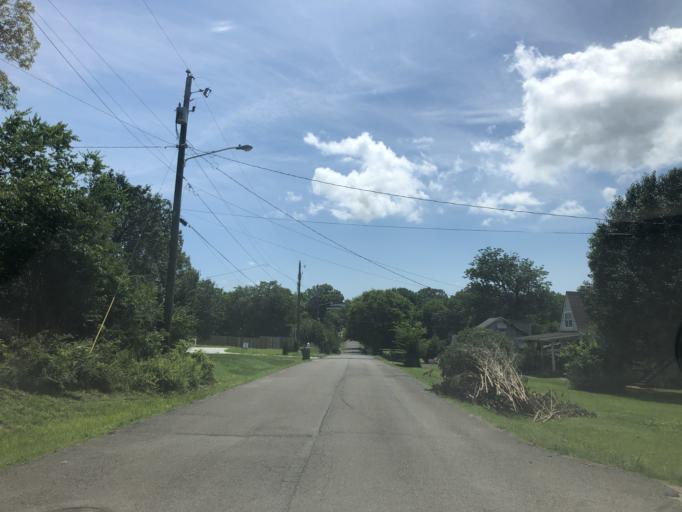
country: US
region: Tennessee
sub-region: Davidson County
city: Lakewood
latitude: 36.2542
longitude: -86.6895
